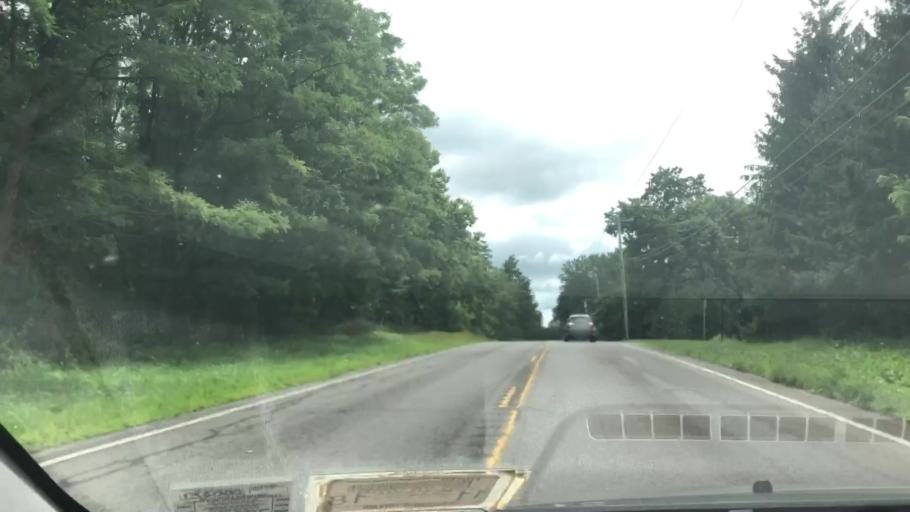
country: US
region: New York
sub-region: Wayne County
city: Macedon
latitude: 43.1224
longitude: -77.2928
